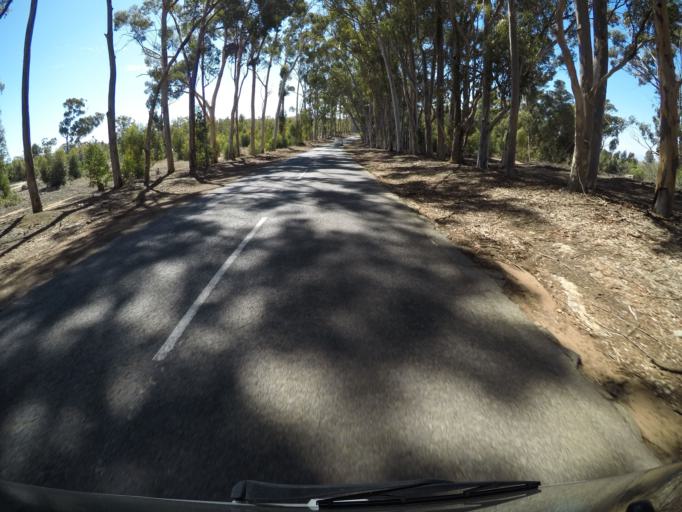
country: ZA
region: Western Cape
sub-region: City of Cape Town
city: Sunset Beach
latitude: -33.7562
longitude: 18.5544
